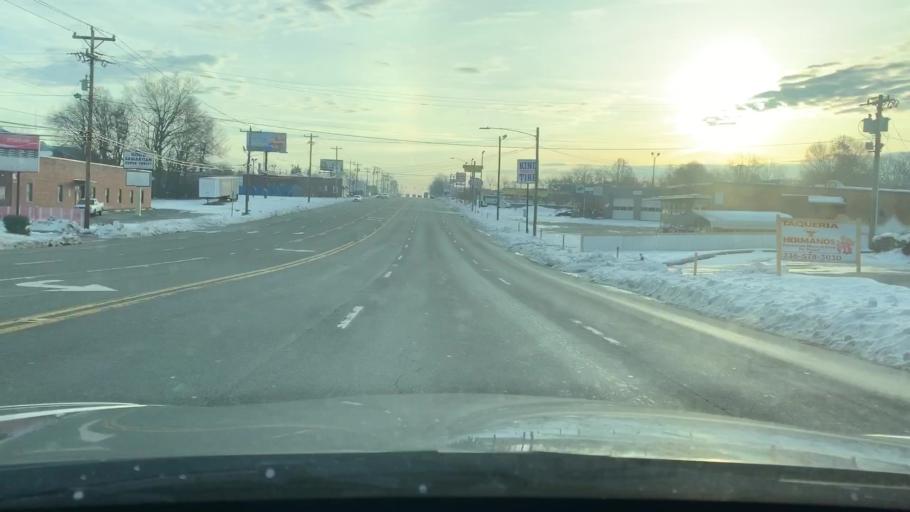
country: US
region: North Carolina
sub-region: Alamance County
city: Burlington
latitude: 36.0963
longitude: -79.4109
